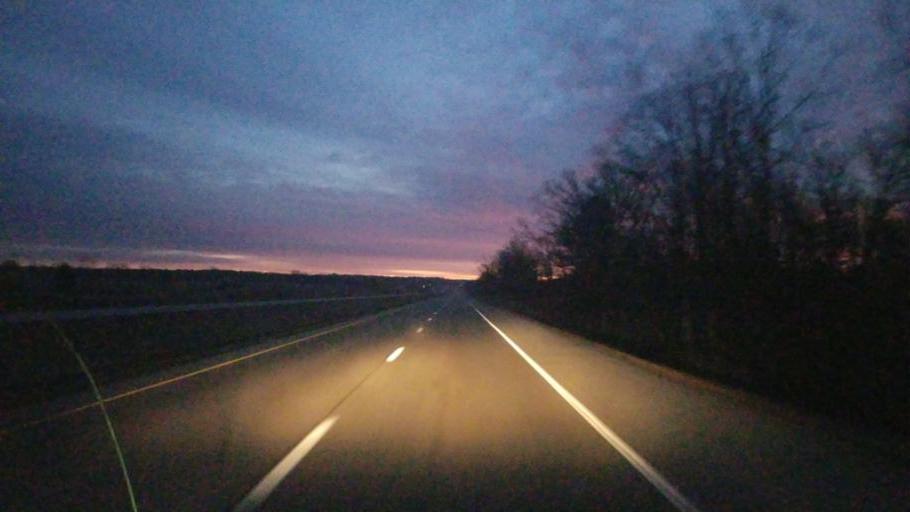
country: US
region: Missouri
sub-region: Howell County
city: Mountain View
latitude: 36.9921
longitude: -91.5193
